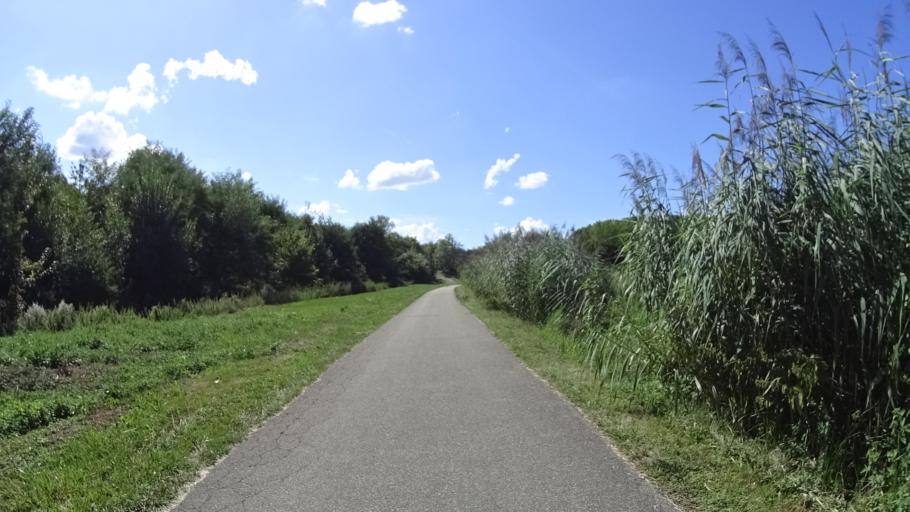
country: FR
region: Alsace
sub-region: Departement du Haut-Rhin
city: Aspach
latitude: 47.6575
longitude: 7.2244
